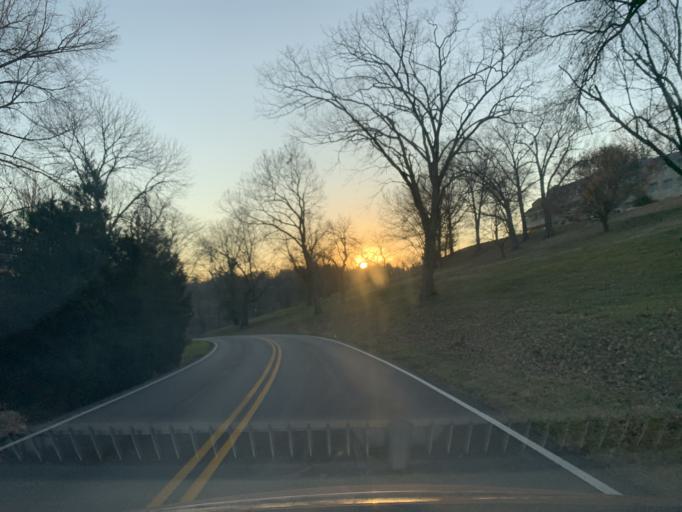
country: US
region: Kentucky
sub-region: Jefferson County
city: Saint Matthews
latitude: 38.2357
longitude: -85.6831
